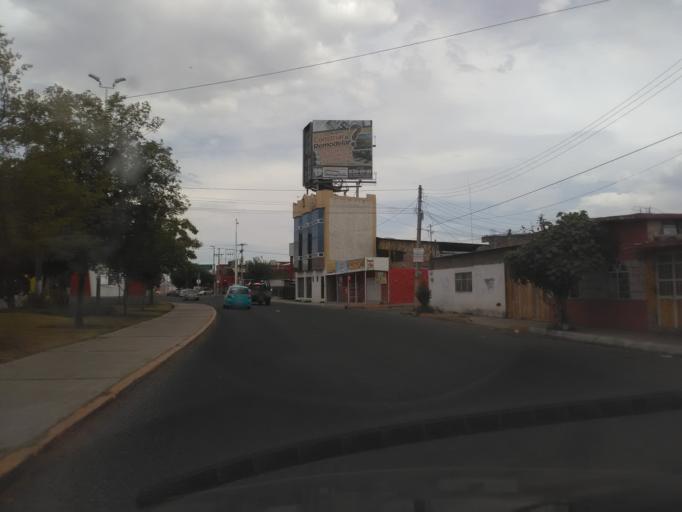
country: MX
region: Durango
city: Victoria de Durango
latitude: 24.0158
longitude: -104.6461
